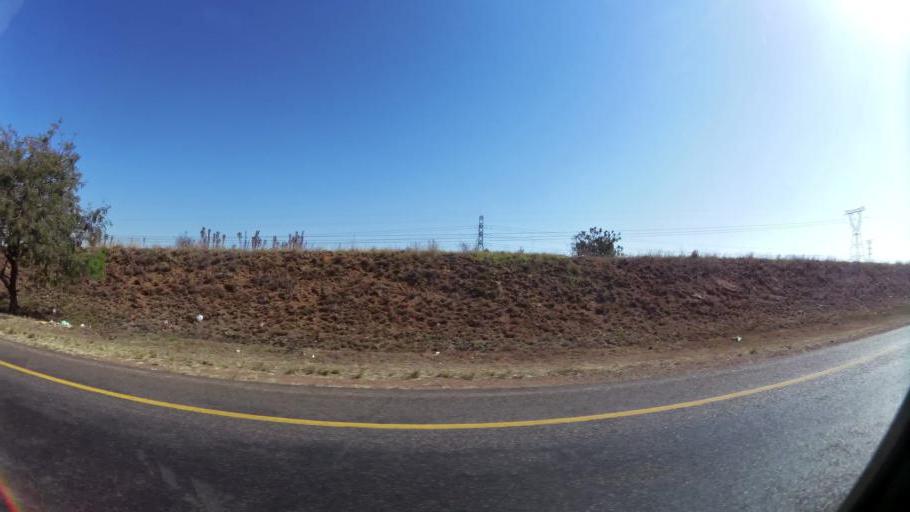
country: ZA
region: Gauteng
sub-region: City of Tshwane Metropolitan Municipality
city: Mabopane
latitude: -25.5468
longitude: 28.1104
